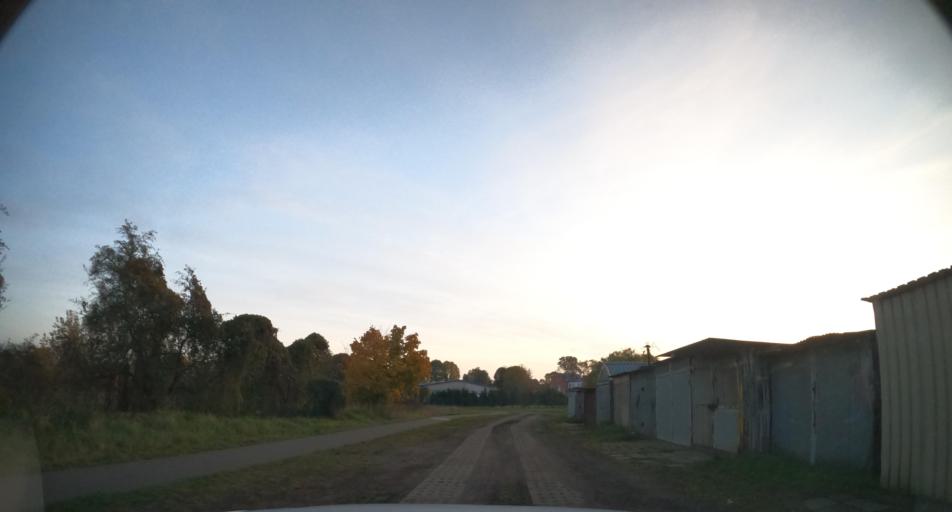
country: PL
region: West Pomeranian Voivodeship
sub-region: Powiat policki
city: Police
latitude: 53.5533
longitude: 14.5648
